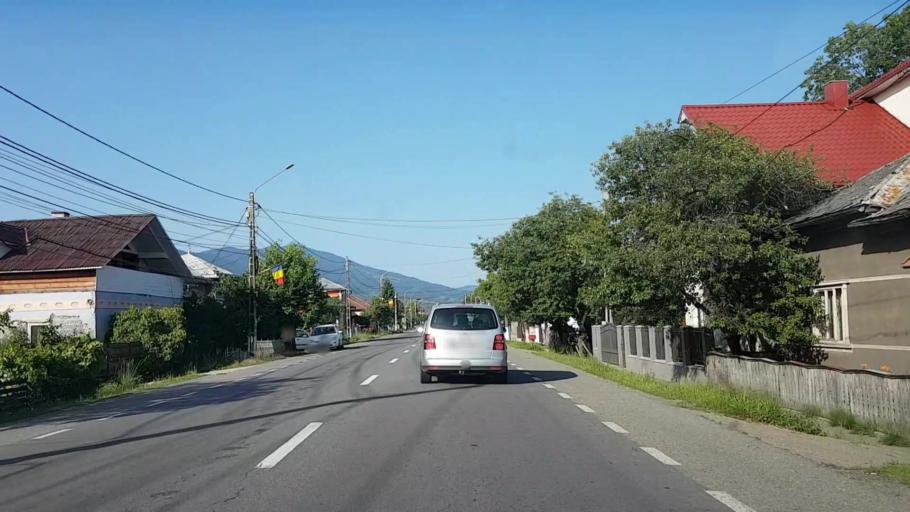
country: RO
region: Bistrita-Nasaud
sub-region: Comuna Josenii Bargaului
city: Josenii Bargaului
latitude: 47.2080
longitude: 24.6610
